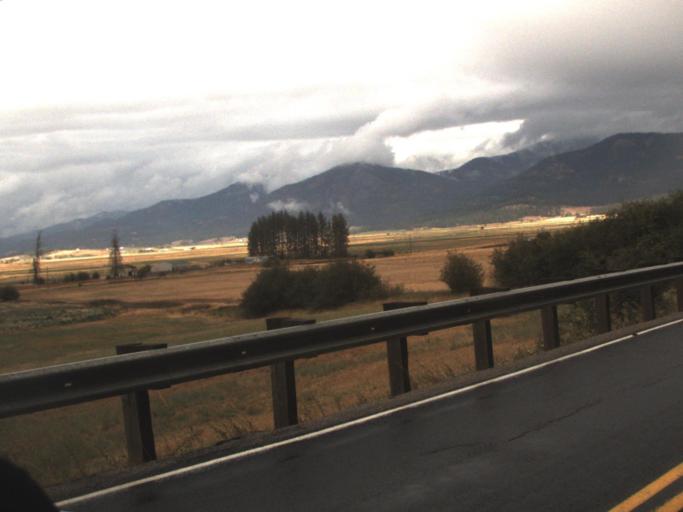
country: US
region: Washington
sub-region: Stevens County
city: Chewelah
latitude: 48.2046
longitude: -117.7265
